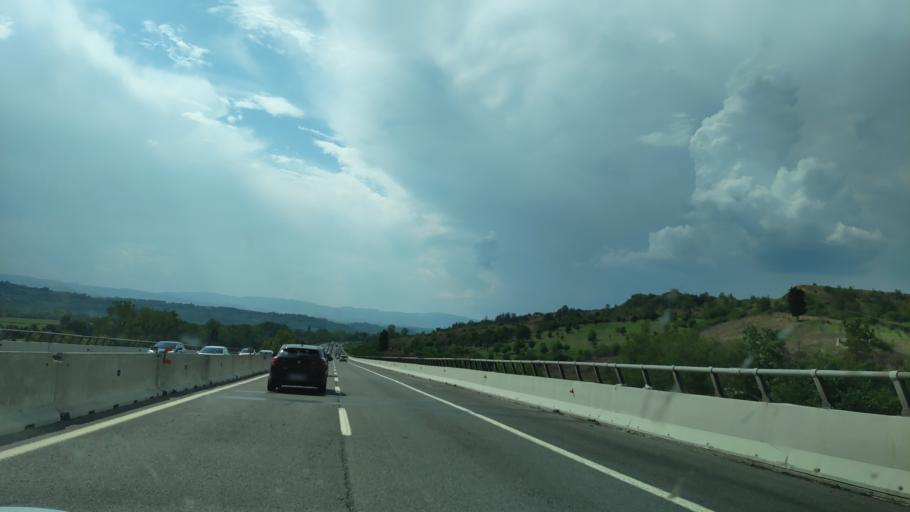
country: IT
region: Tuscany
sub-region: Province of Arezzo
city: Bucine
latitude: 43.5144
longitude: 11.6267
